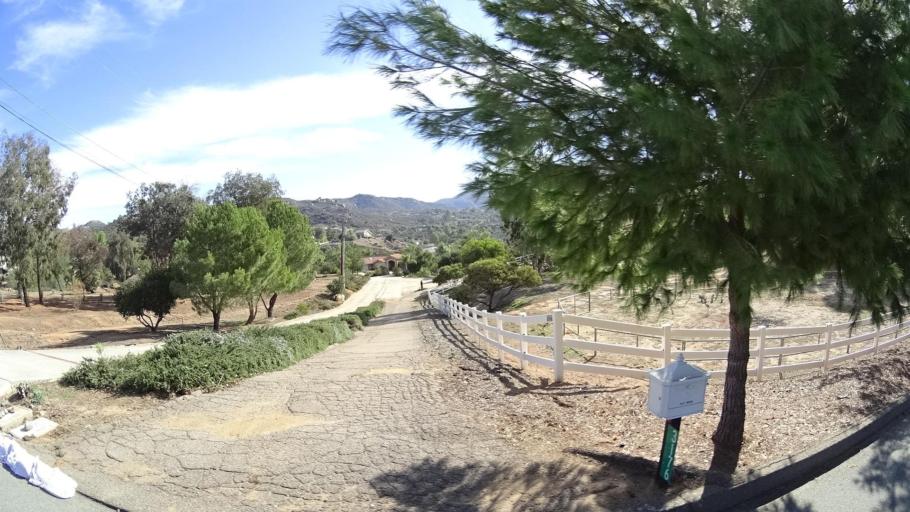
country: US
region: California
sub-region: San Diego County
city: Alpine
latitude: 32.8151
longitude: -116.7458
